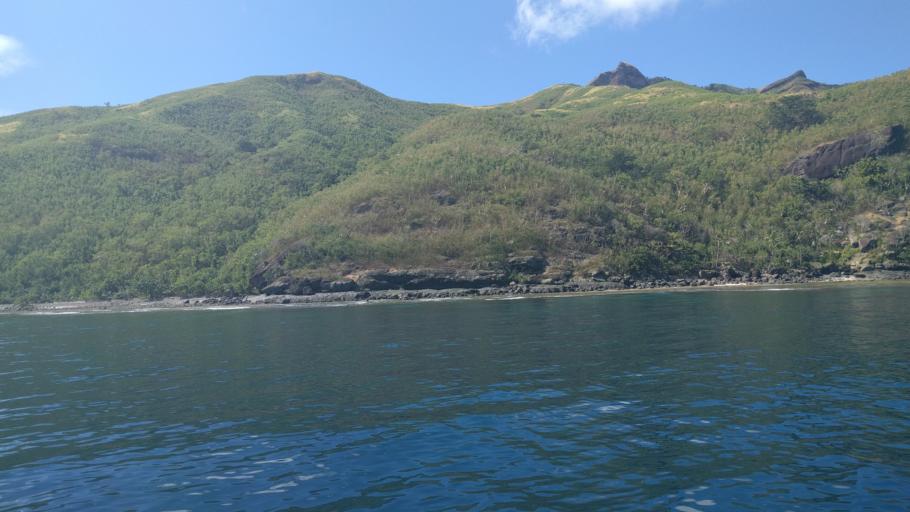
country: FJ
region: Western
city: Lautoka
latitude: -17.2854
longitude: 177.1022
